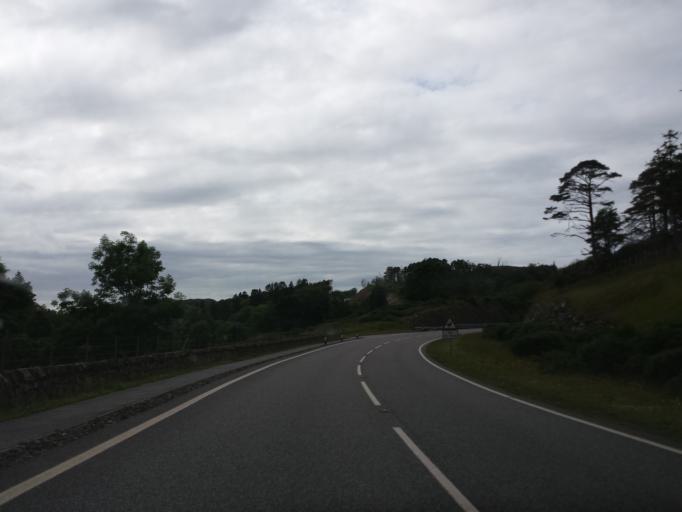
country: GB
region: Scotland
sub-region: Argyll and Bute
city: Isle Of Mull
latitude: 56.8989
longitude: -5.7823
